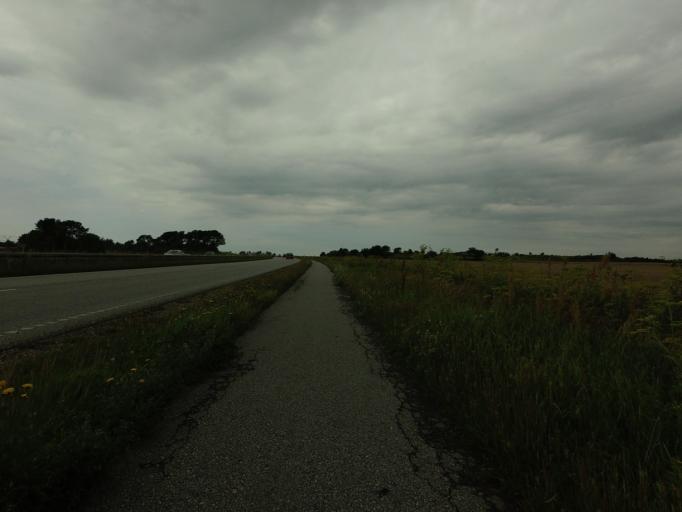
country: DK
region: North Denmark
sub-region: Alborg Kommune
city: Vadum
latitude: 57.1059
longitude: 9.8801
